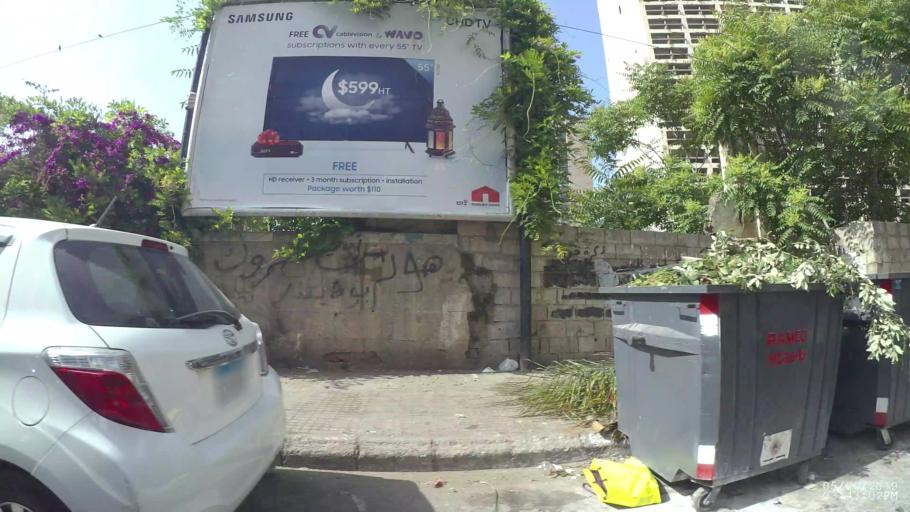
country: LB
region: Beyrouth
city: Beirut
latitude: 33.8992
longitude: 35.4941
